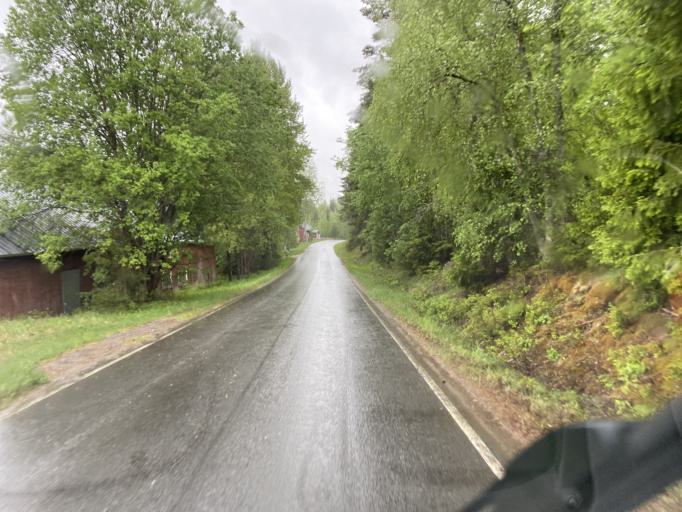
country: FI
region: Haeme
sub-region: Forssa
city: Humppila
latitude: 61.0721
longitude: 23.3137
